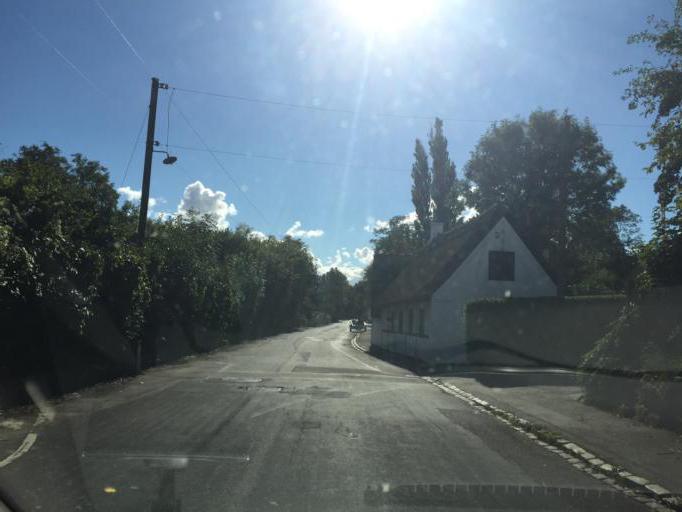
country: DK
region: Zealand
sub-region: Roskilde Kommune
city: Roskilde
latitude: 55.6775
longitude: 12.0875
